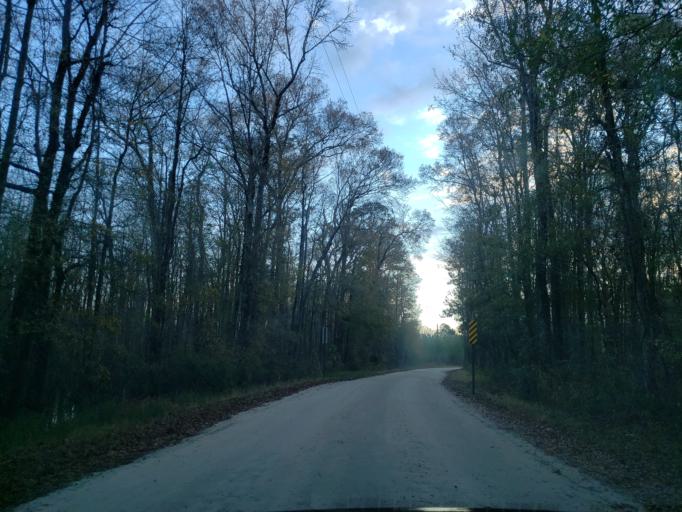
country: US
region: Georgia
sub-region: Chatham County
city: Bloomingdale
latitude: 32.1197
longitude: -81.3363
